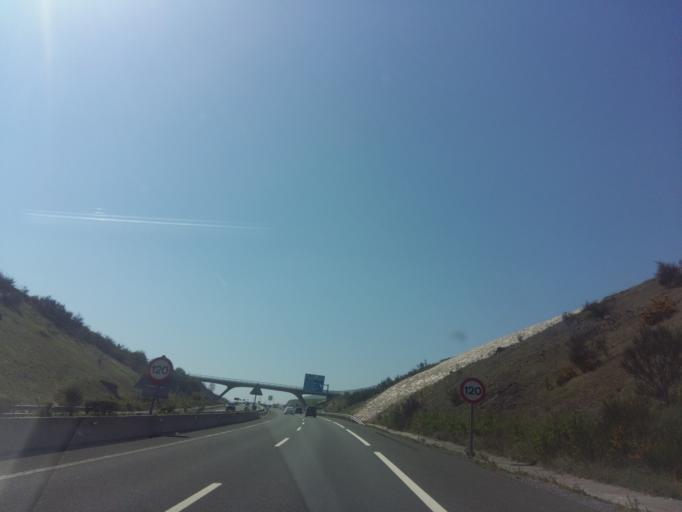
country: ES
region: Cantabria
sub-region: Provincia de Cantabria
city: Pesquera
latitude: 43.0793
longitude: -4.0861
